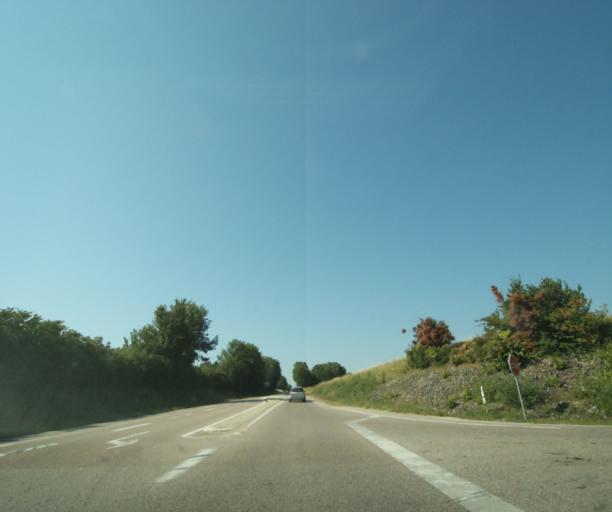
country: FR
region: Lorraine
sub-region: Departement de Meurthe-et-Moselle
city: Toul
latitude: 48.6614
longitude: 5.8777
